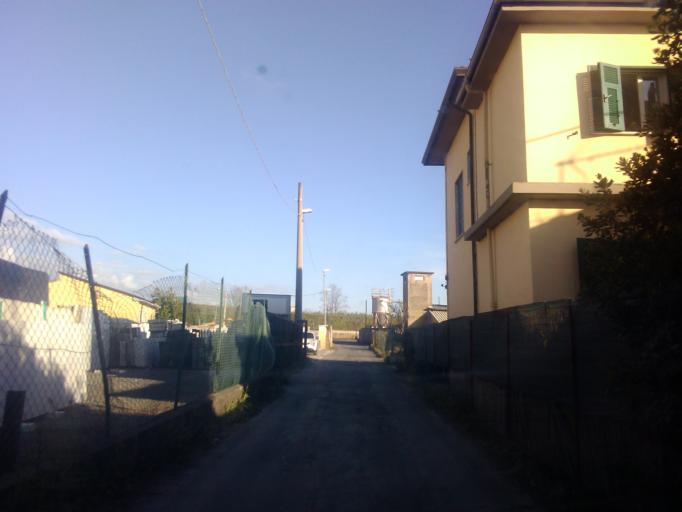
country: IT
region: Tuscany
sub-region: Provincia di Massa-Carrara
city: Carrara
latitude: 44.0421
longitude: 10.0580
